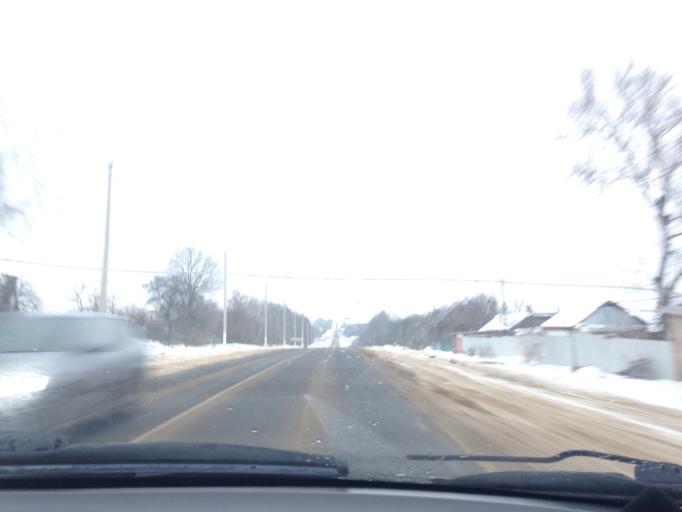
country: RU
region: Tula
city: Shchekino
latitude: 53.9636
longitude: 37.4951
